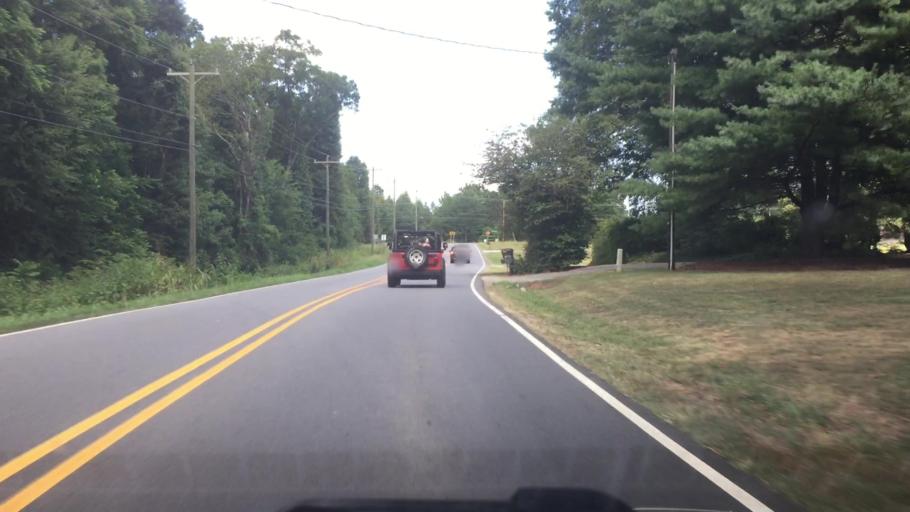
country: US
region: North Carolina
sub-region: Rowan County
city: Enochville
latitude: 35.4333
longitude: -80.7270
